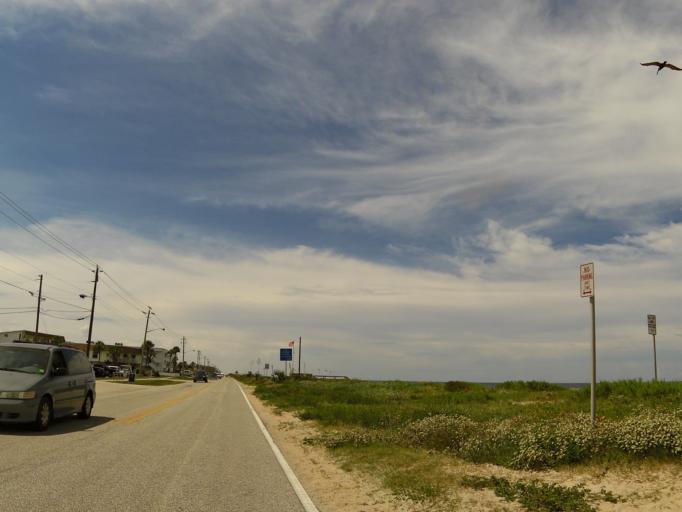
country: US
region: Florida
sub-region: Volusia County
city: Ormond-by-the-Sea
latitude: 29.3405
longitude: -81.0623
